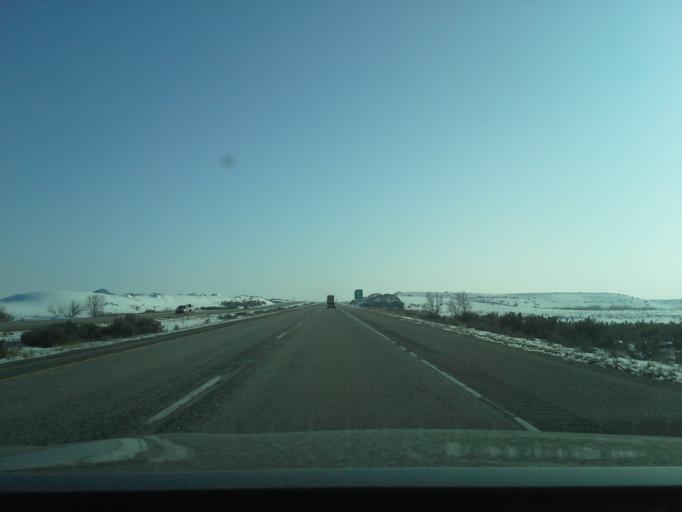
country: US
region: Idaho
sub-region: Oneida County
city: Malad City
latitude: 42.5231
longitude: -112.1709
